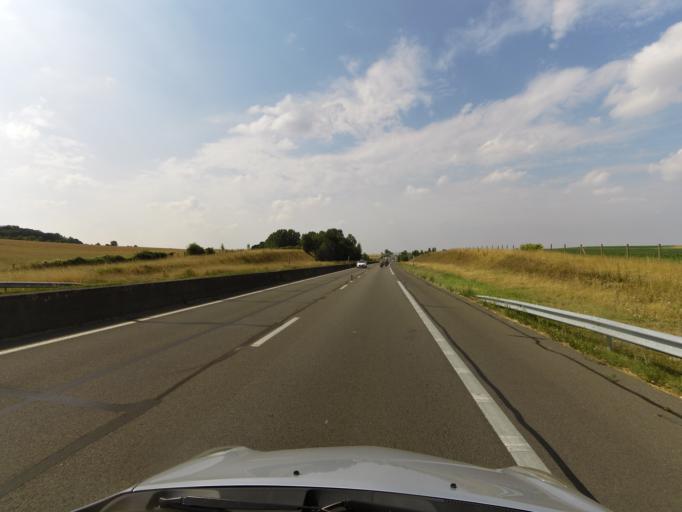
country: FR
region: Picardie
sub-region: Departement de l'Aisne
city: Itancourt
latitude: 49.7643
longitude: 3.3600
